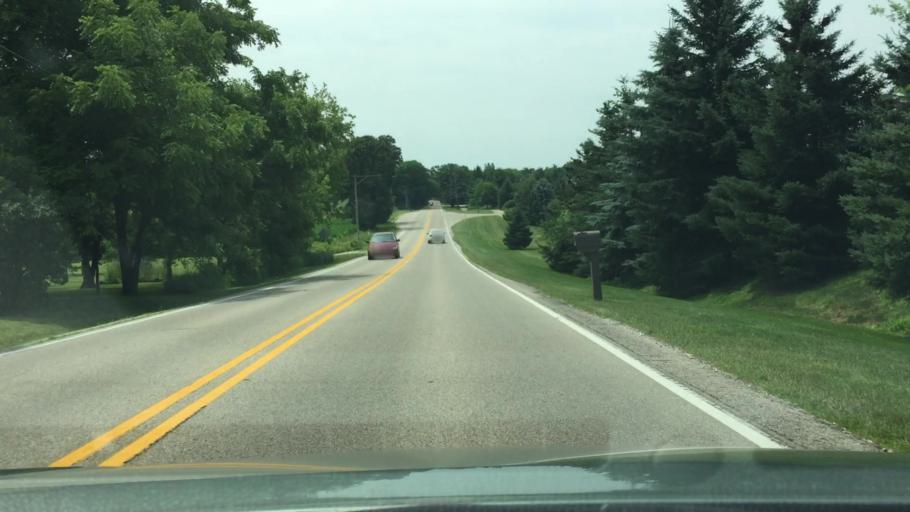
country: US
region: Wisconsin
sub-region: Waukesha County
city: Merton
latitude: 43.1333
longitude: -88.3076
